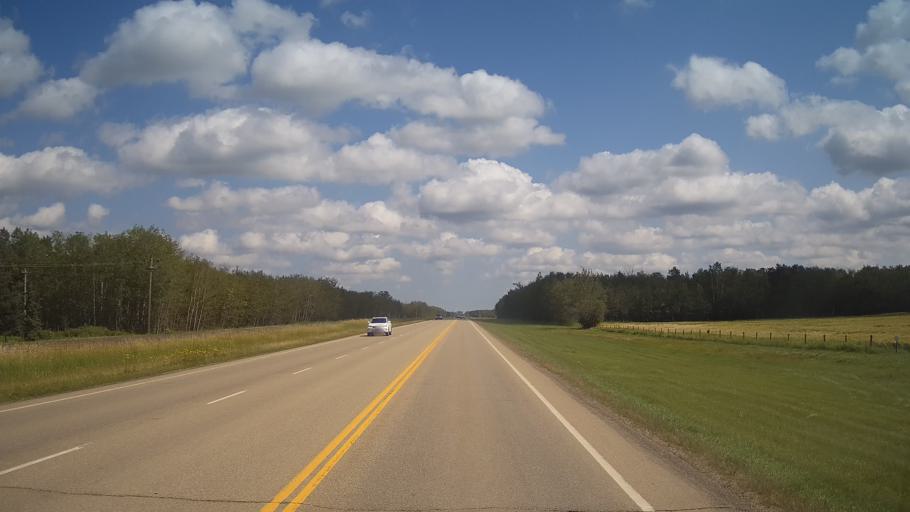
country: CA
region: Alberta
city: Sherwood Park
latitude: 53.3957
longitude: -113.0584
